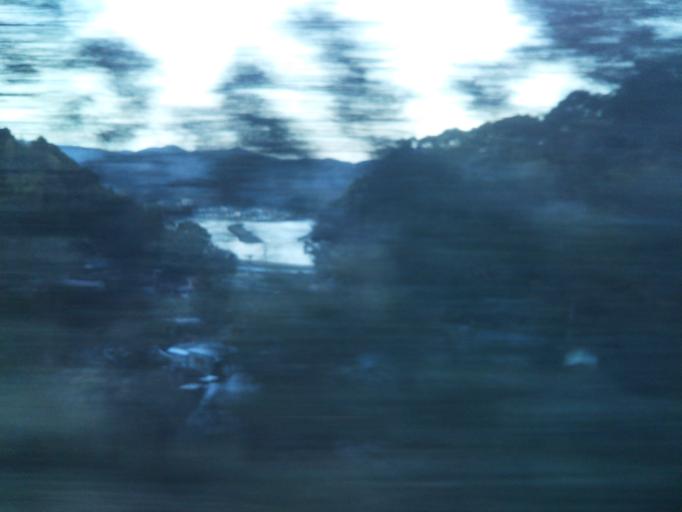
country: JP
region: Kochi
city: Susaki
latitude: 33.3202
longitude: 133.2320
